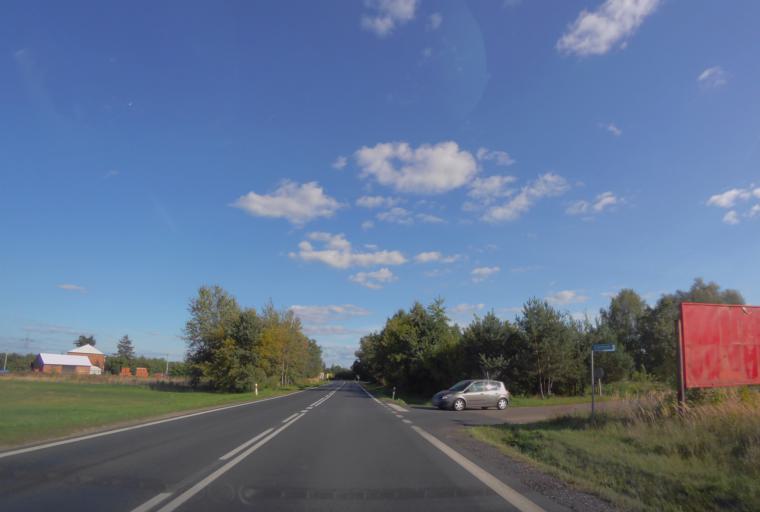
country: PL
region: Subcarpathian Voivodeship
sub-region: Tarnobrzeg
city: Tarnobrzeg
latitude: 50.5585
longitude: 21.7499
